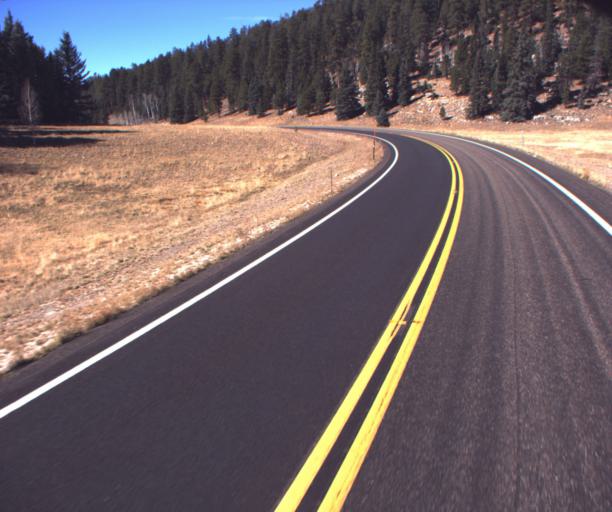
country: US
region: Arizona
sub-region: Coconino County
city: Grand Canyon
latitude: 36.5406
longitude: -112.1581
